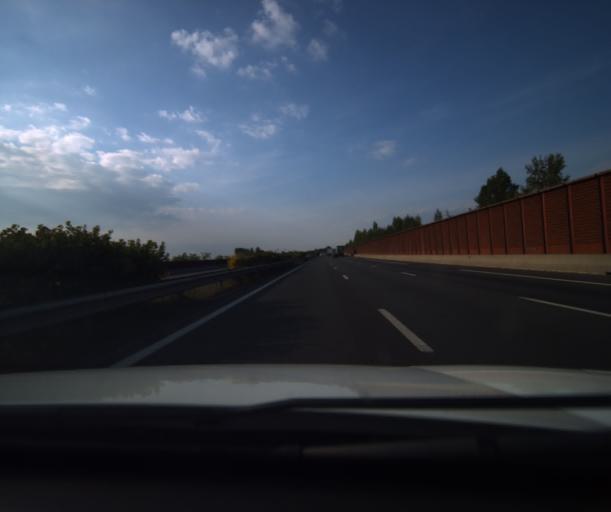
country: FR
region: Midi-Pyrenees
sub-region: Departement de la Haute-Garonne
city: Bouloc
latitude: 43.7724
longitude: 1.3842
